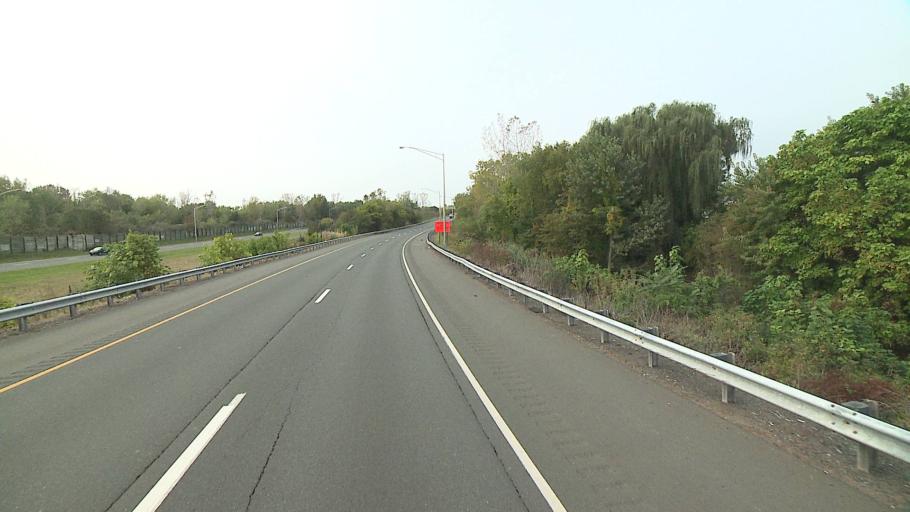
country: US
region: Connecticut
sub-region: Hartford County
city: New Britain
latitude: 41.6850
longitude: -72.7577
